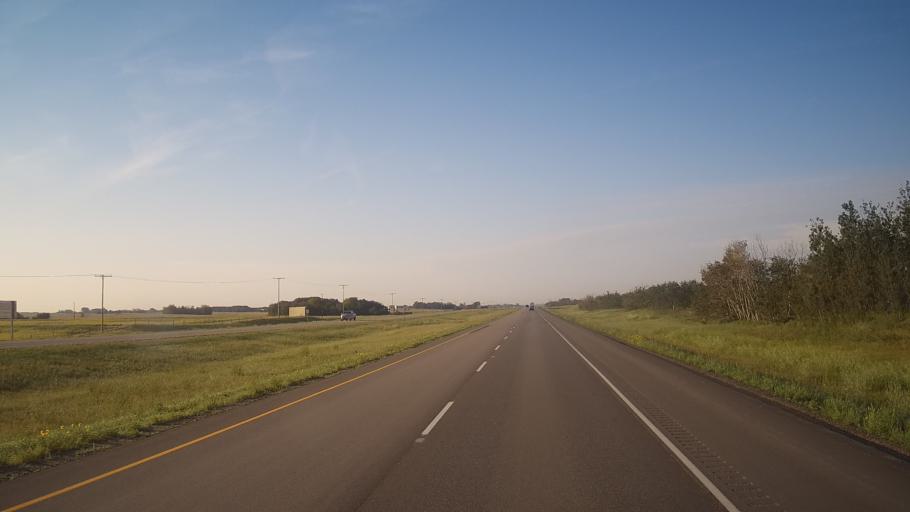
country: CA
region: Saskatchewan
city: Saskatoon
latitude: 52.0435
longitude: -106.5917
